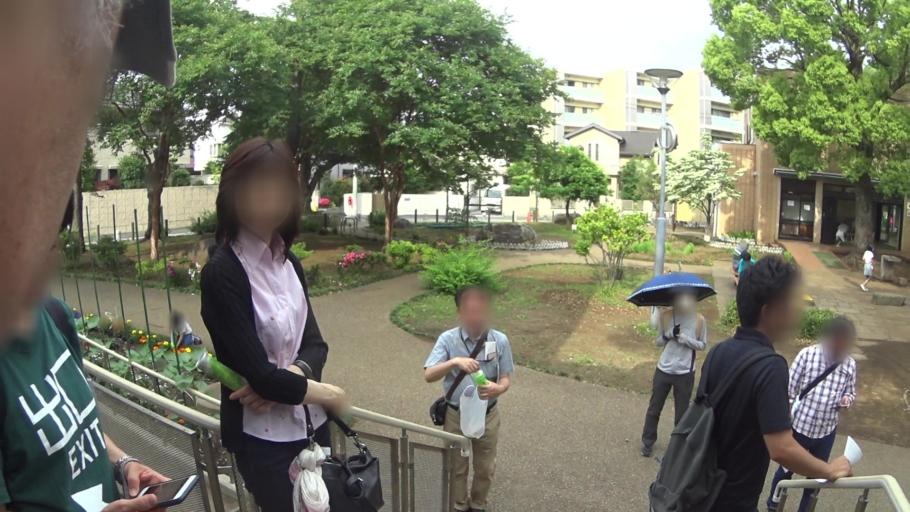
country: JP
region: Tokyo
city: Musashino
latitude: 35.7088
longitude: 139.6213
